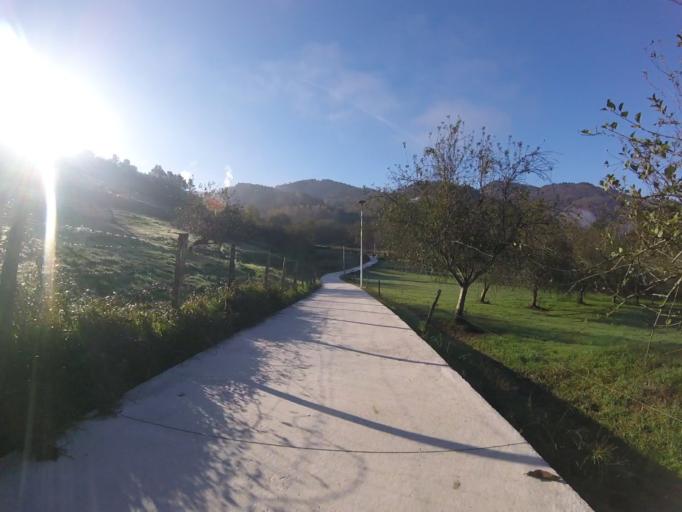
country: ES
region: Basque Country
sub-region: Provincia de Guipuzcoa
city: Usurbil
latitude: 43.2644
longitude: -2.0420
